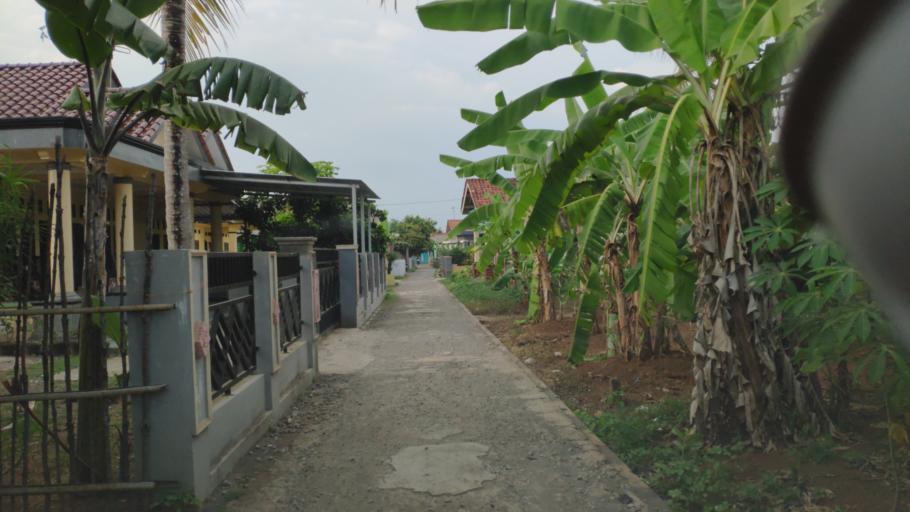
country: ID
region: Central Java
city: Karangbadar Kidul
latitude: -7.7086
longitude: 108.9712
